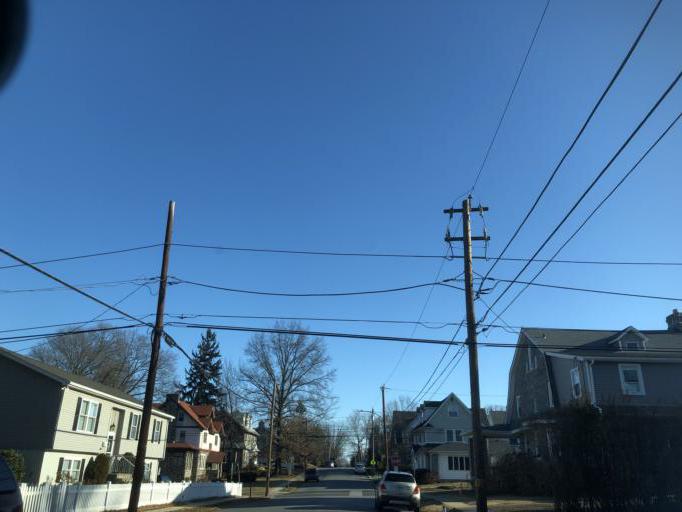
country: US
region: Pennsylvania
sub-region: Delaware County
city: Drexel Hill
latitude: 39.9482
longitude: -75.2958
